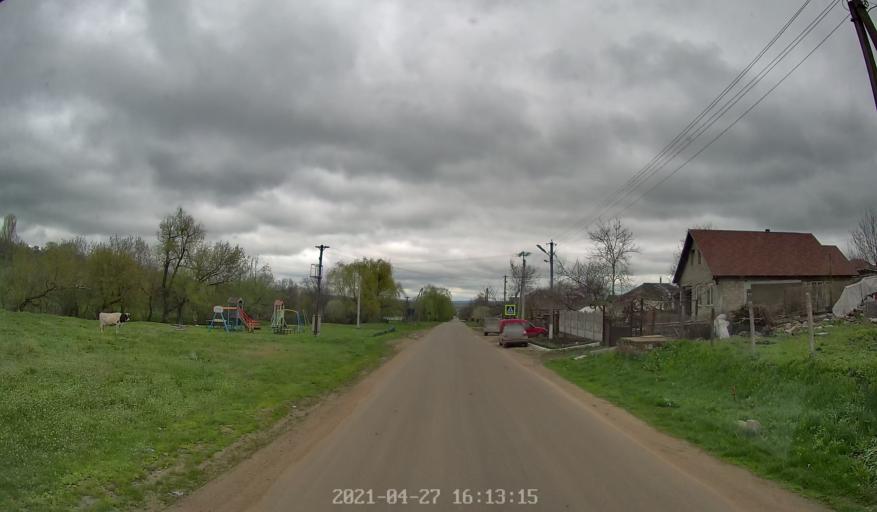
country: MD
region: Chisinau
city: Vadul lui Voda
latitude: 47.0098
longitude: 29.0121
